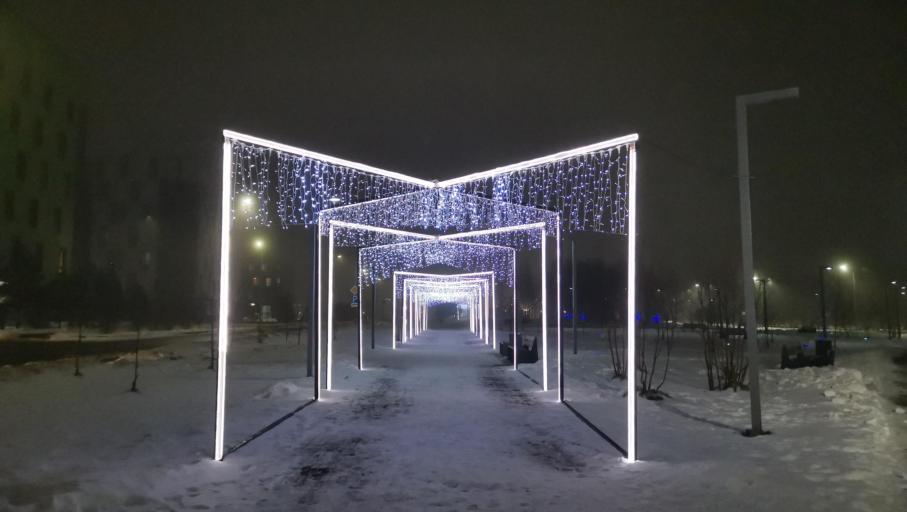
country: RU
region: Tatarstan
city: Sviyazhsk
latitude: 55.7472
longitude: 48.7412
